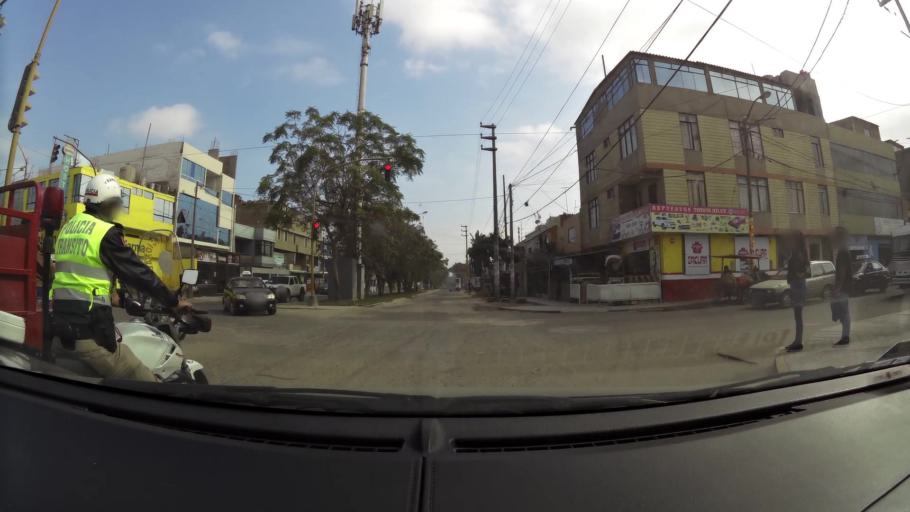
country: PE
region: La Libertad
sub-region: Provincia de Trujillo
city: Trujillo
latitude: -8.1072
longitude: -79.0149
